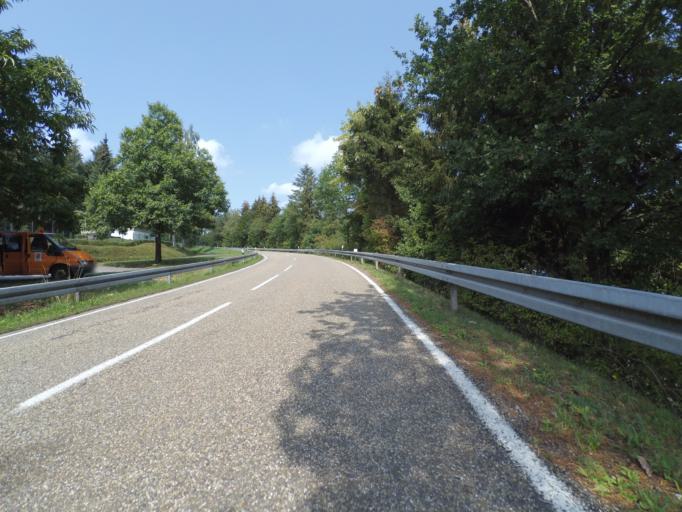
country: DE
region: Saarland
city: Britten
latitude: 49.5095
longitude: 6.6922
